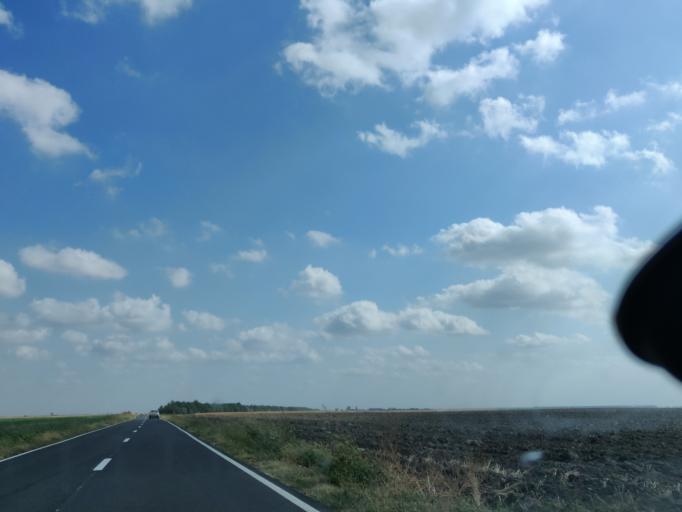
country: RO
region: Vrancea
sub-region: Comuna Ciorasti
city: Mihalceni
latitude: 45.4473
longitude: 27.3553
